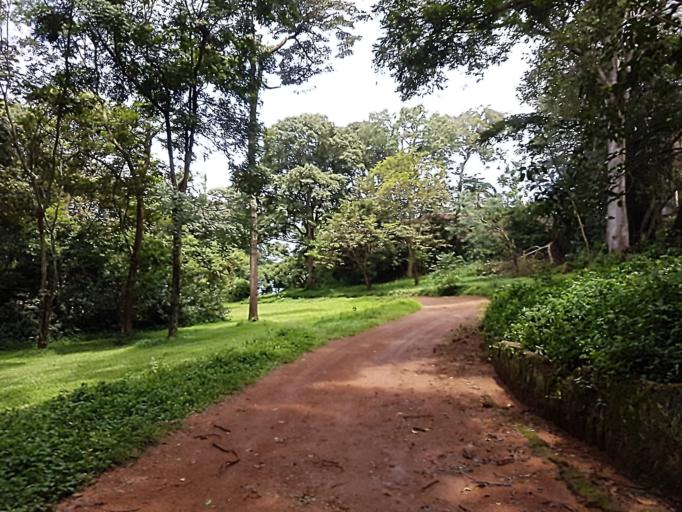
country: UG
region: Central Region
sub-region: Wakiso District
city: Entebbe
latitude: 0.0600
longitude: 32.4801
